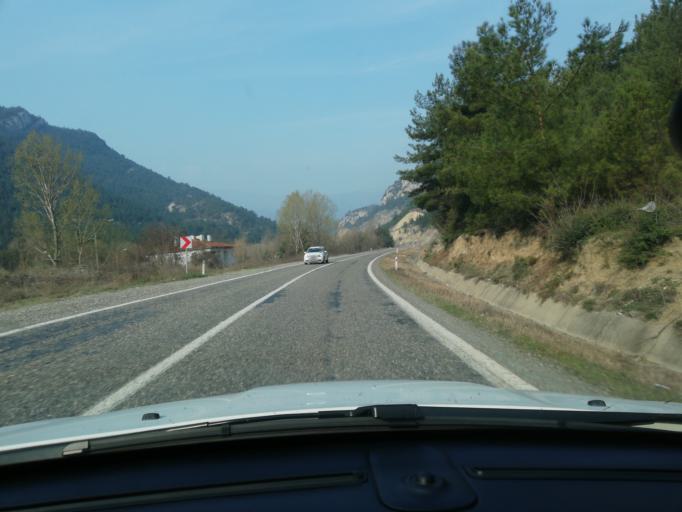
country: TR
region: Karabuk
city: Karabuk
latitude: 41.1605
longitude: 32.5649
